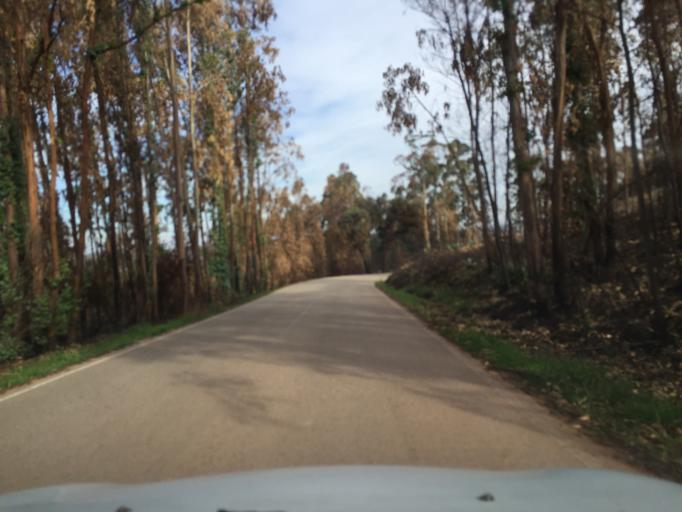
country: PT
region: Aveiro
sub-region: Anadia
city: Anadia
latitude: 40.3991
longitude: -8.3959
